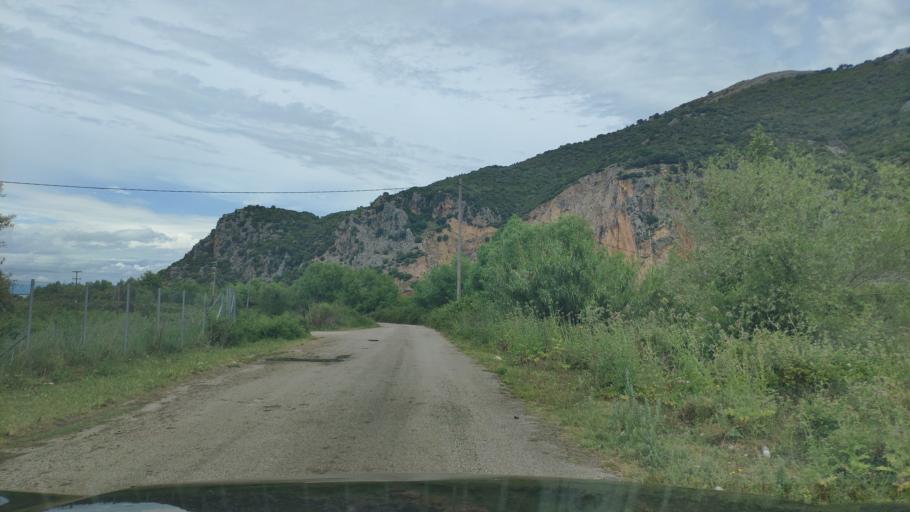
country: GR
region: West Greece
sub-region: Nomos Aitolias kai Akarnanias
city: Vonitsa
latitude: 38.9121
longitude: 20.9079
